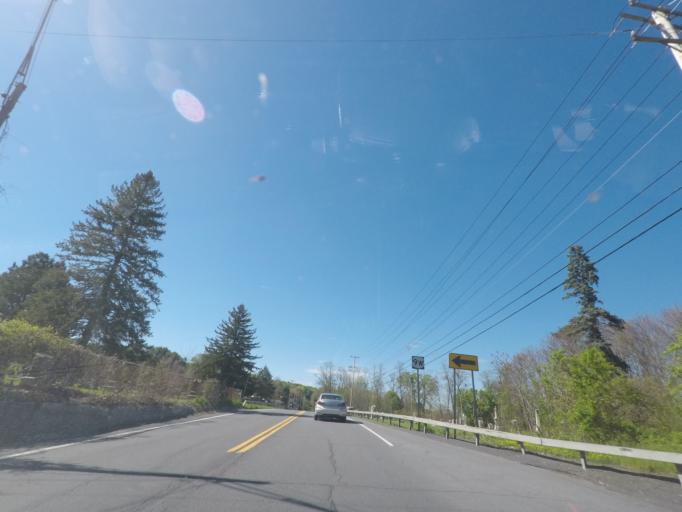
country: US
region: New York
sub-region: Albany County
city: Ravena
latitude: 42.4478
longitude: -73.8146
